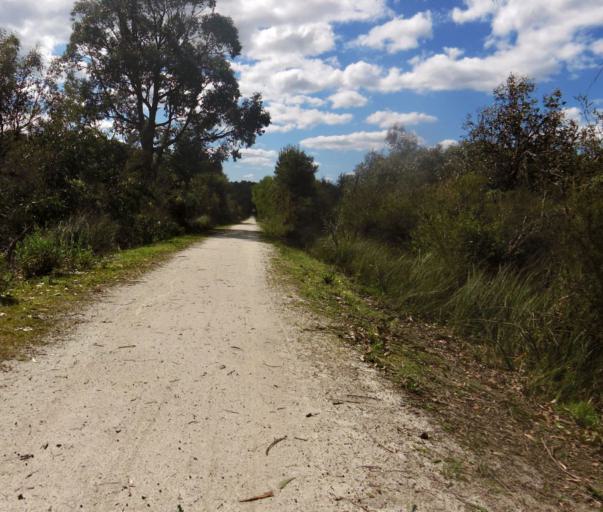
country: AU
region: Victoria
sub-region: Bass Coast
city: North Wonthaggi
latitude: -38.6136
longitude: 146.0432
